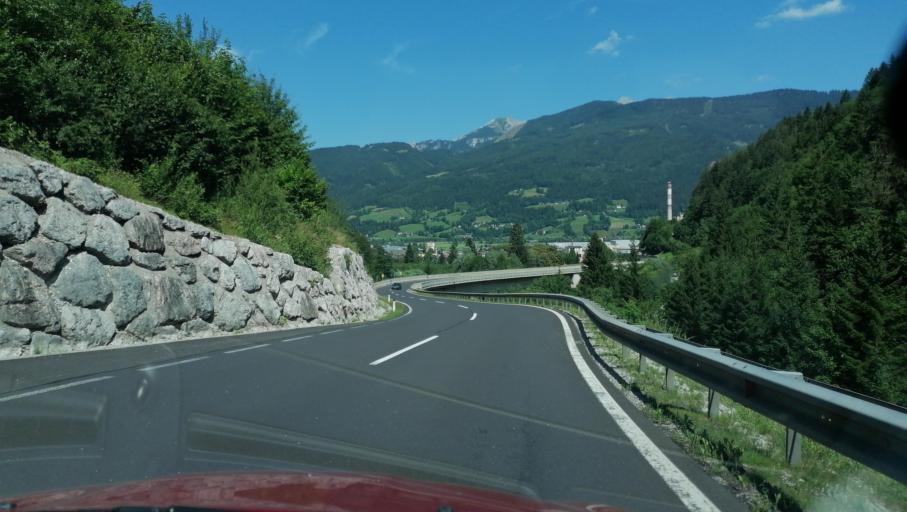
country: AT
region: Styria
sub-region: Politischer Bezirk Liezen
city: Trieben
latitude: 47.4759
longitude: 14.4839
